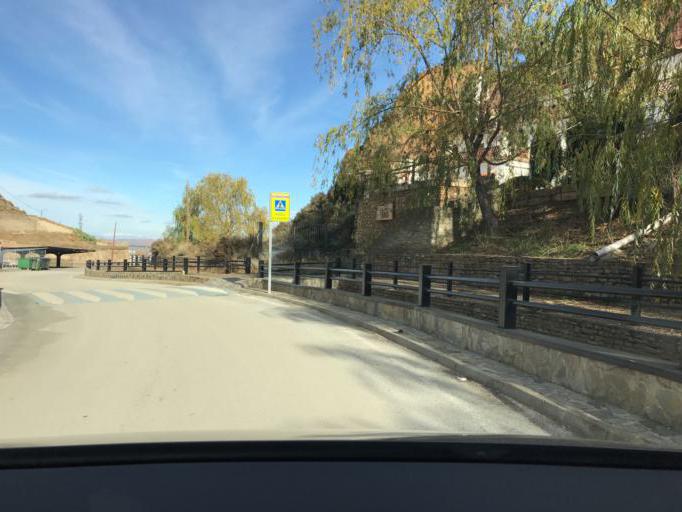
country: ES
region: Andalusia
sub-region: Provincia de Granada
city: Marchal
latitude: 37.3035
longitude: -3.2090
